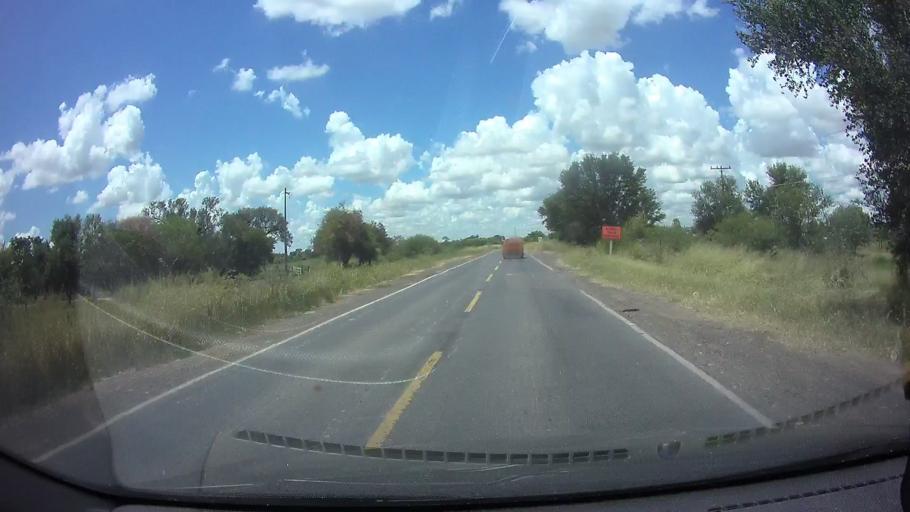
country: PY
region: Central
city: Colonia Mariano Roque Alonso
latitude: -25.1883
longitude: -57.6033
